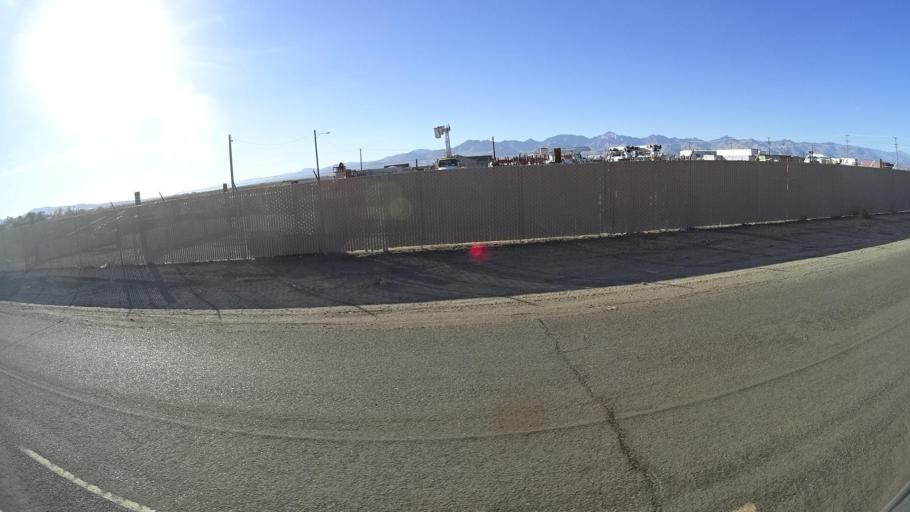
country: US
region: California
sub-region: Kern County
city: Ridgecrest
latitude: 35.6505
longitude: -117.7054
